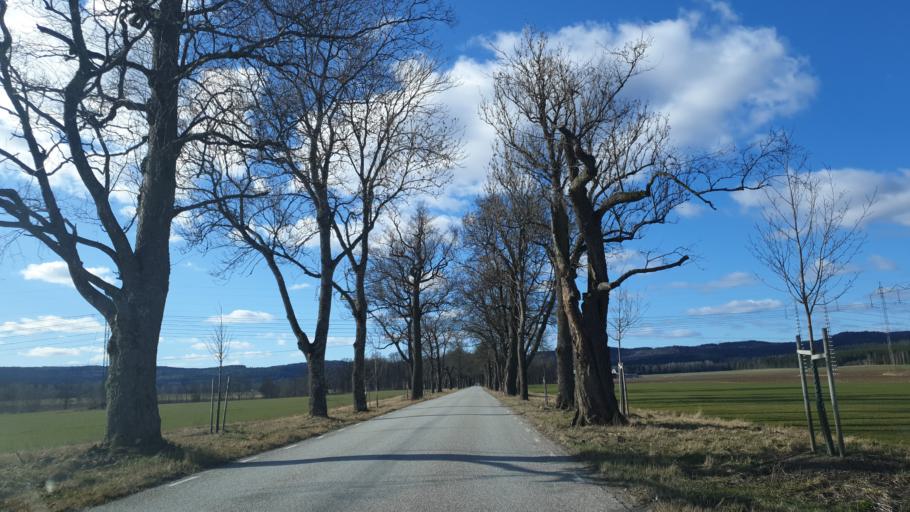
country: SE
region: OErebro
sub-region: Orebro Kommun
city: Garphyttan
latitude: 59.3396
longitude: 15.0257
